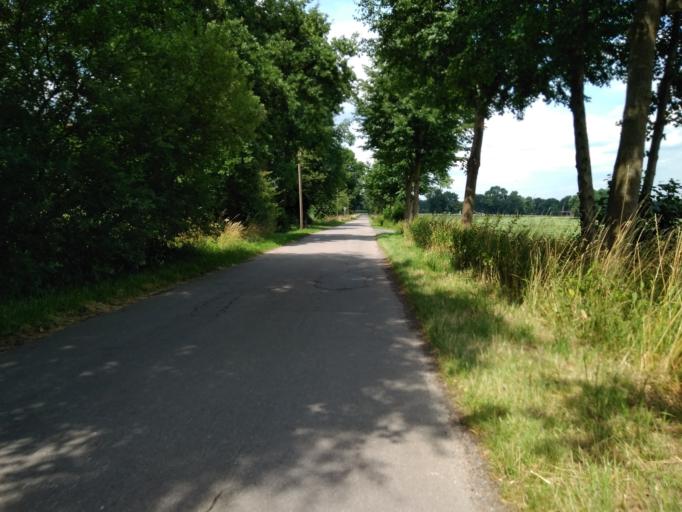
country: DE
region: North Rhine-Westphalia
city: Dorsten
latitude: 51.6229
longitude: 6.9662
